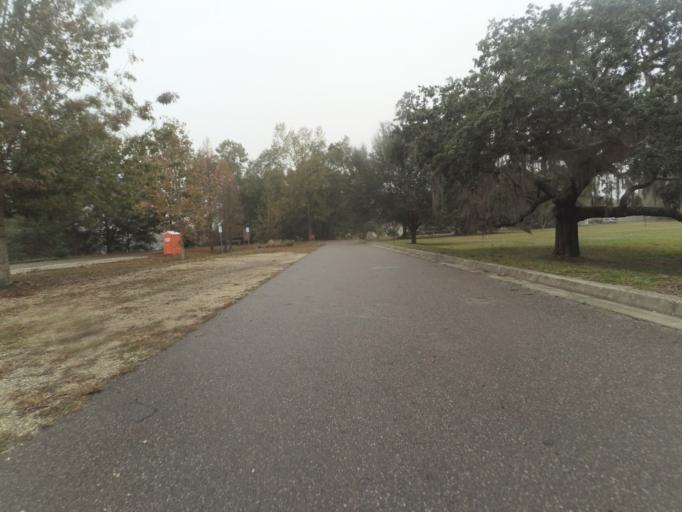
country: US
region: Florida
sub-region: Alachua County
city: Hawthorne
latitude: 29.5875
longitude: -82.0891
